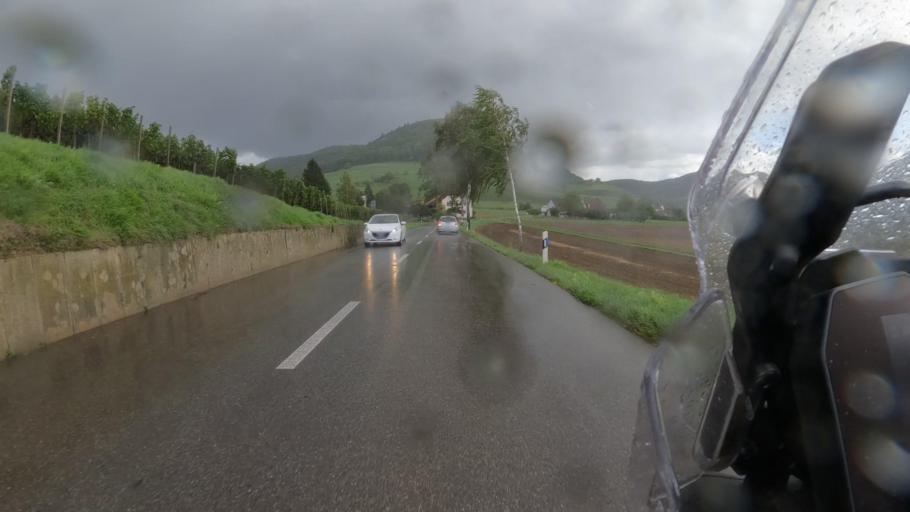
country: CH
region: Schaffhausen
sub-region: Bezirk Unterklettgau
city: Wilchingen
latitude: 47.6610
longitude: 8.4769
